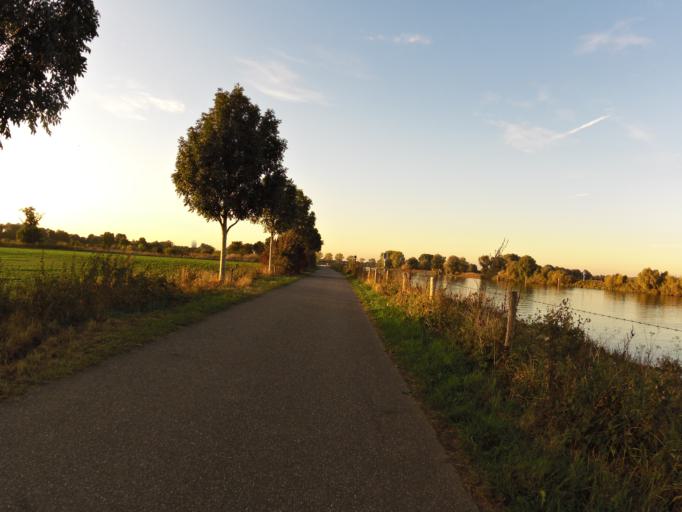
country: NL
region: North Brabant
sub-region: Gemeente Boxmeer
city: Boxmeer
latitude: 51.6441
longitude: 5.9721
